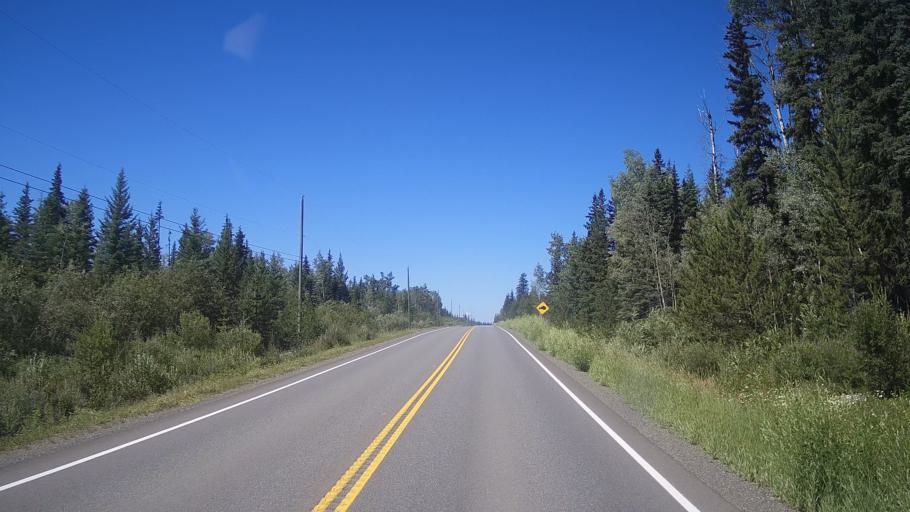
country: CA
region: British Columbia
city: Cache Creek
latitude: 51.5414
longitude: -120.9705
